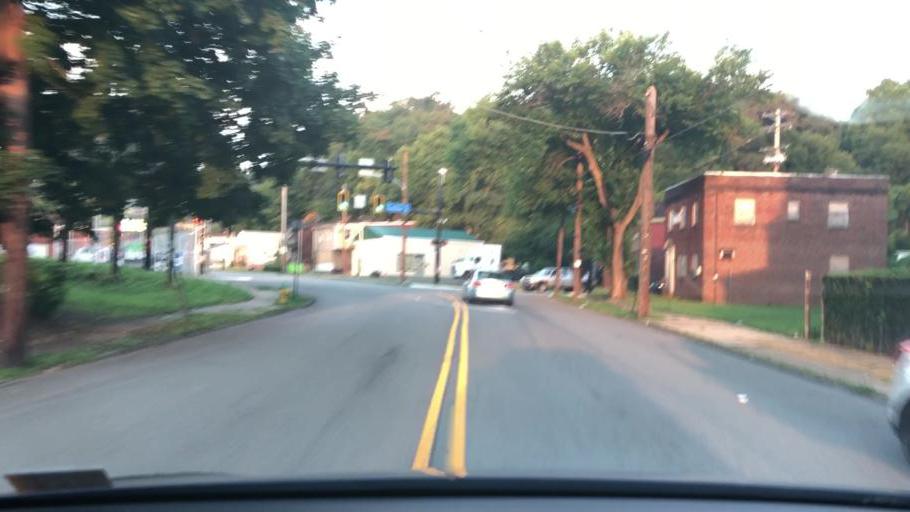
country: US
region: Pennsylvania
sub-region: Allegheny County
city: Wilkinsburg
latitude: 40.4541
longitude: -79.8862
